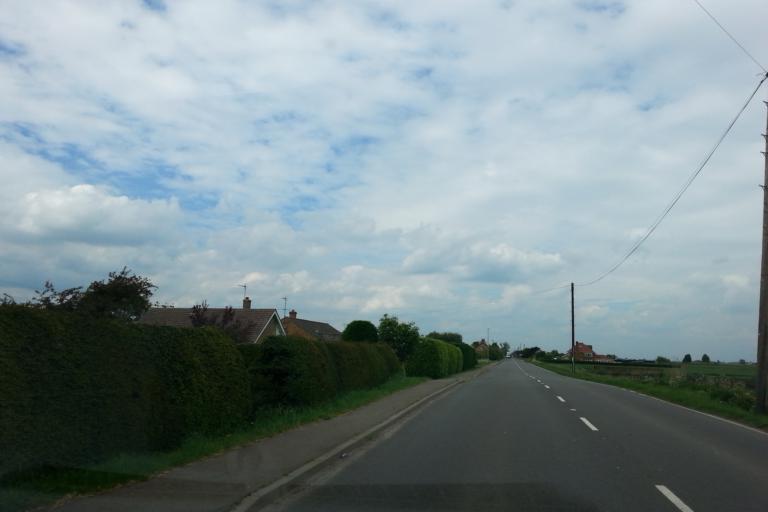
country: GB
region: England
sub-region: Cambridgeshire
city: Ramsey
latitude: 52.4718
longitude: -0.1531
